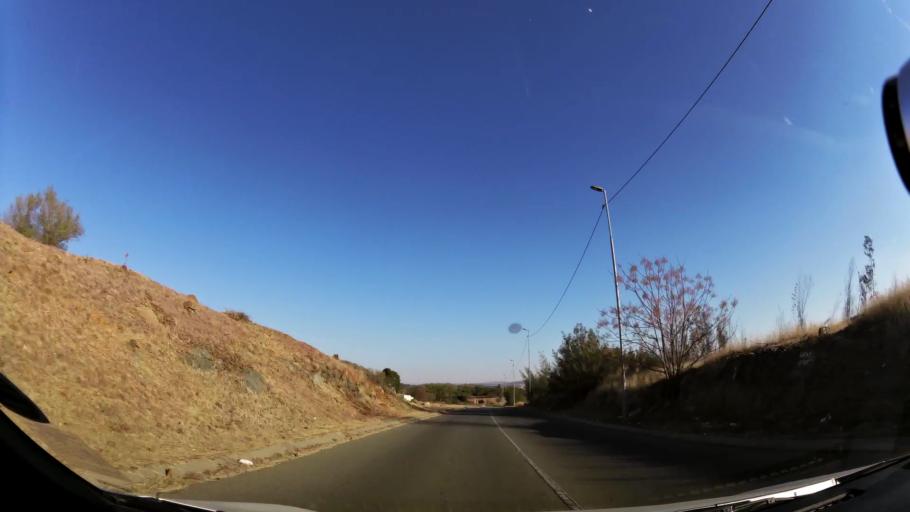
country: ZA
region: Gauteng
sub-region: City of Johannesburg Metropolitan Municipality
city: Johannesburg
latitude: -26.2963
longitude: 28.0728
